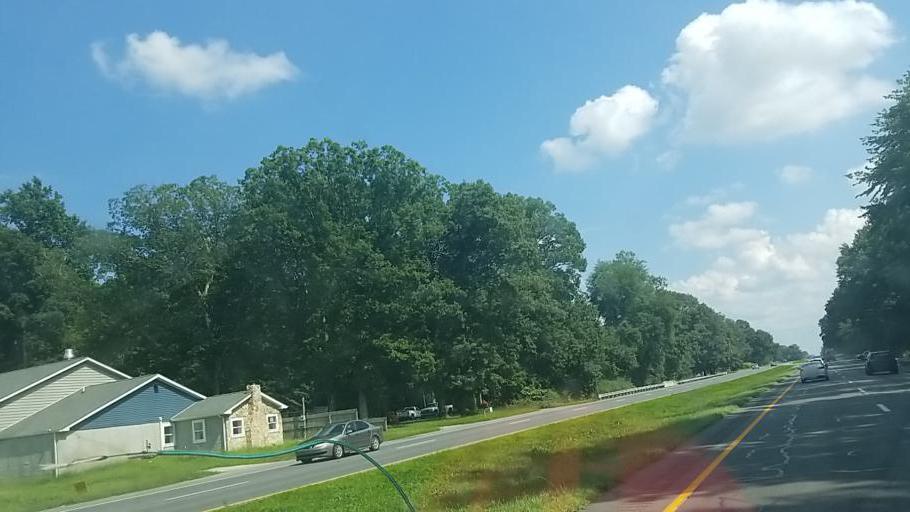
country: US
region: Delaware
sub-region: Sussex County
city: Georgetown
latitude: 38.6488
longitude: -75.3642
